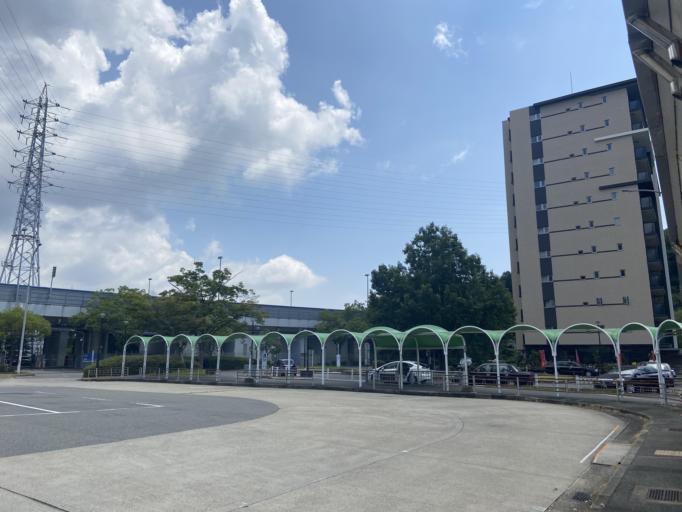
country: JP
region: Hyogo
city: Kobe
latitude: 34.6753
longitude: 135.1102
